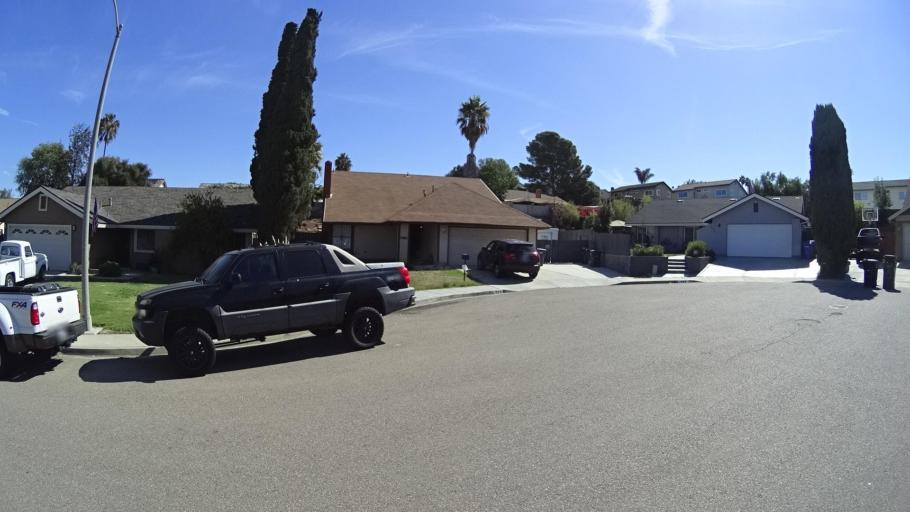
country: US
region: California
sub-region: San Diego County
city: La Presa
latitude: 32.7052
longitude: -117.0059
